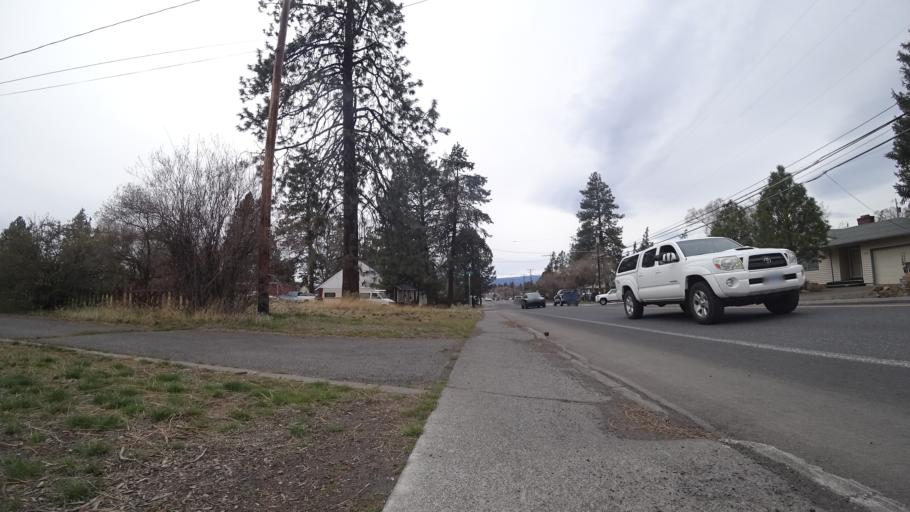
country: US
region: Oregon
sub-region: Deschutes County
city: Bend
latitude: 44.0559
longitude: -121.2985
